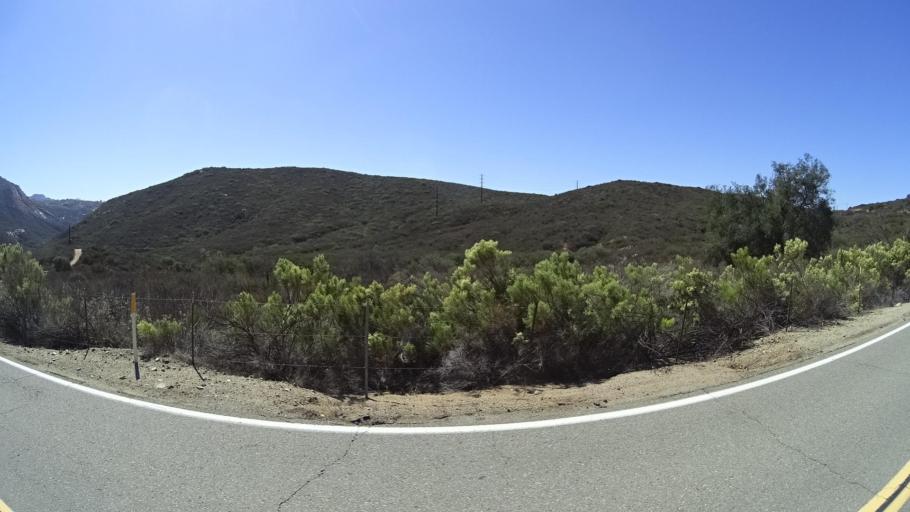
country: US
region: California
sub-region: San Diego County
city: Alpine
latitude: 32.8018
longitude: -116.7637
